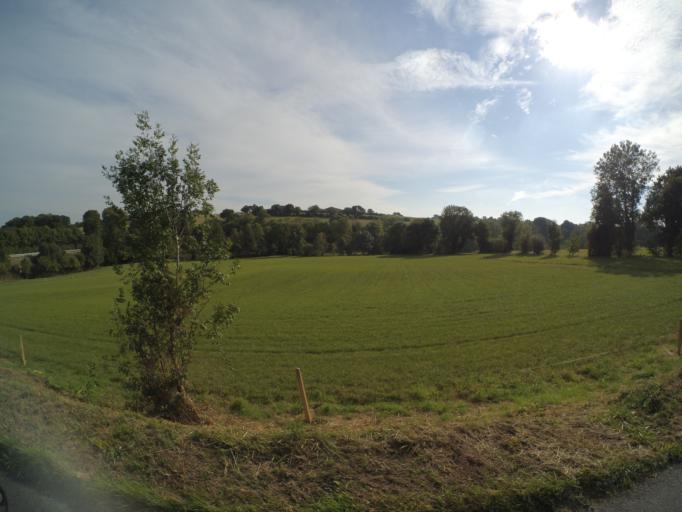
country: FR
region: Pays de la Loire
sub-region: Departement de Maine-et-Loire
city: La Chapelle-du-Genet
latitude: 47.1883
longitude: -1.0339
